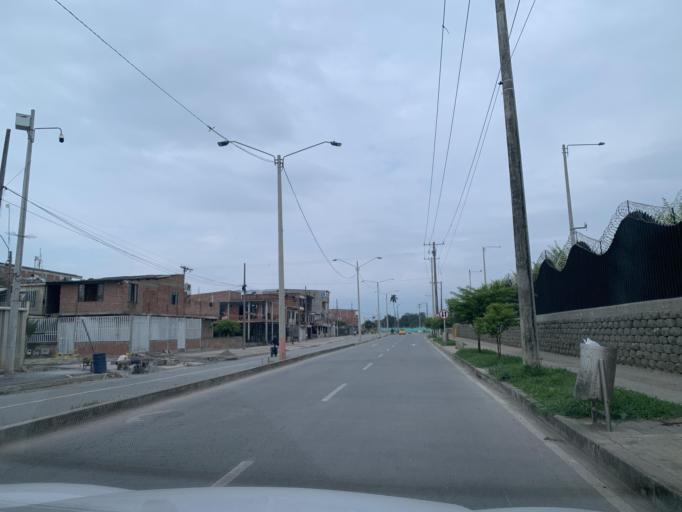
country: CO
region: Valle del Cauca
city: Cali
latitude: 3.4105
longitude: -76.4757
